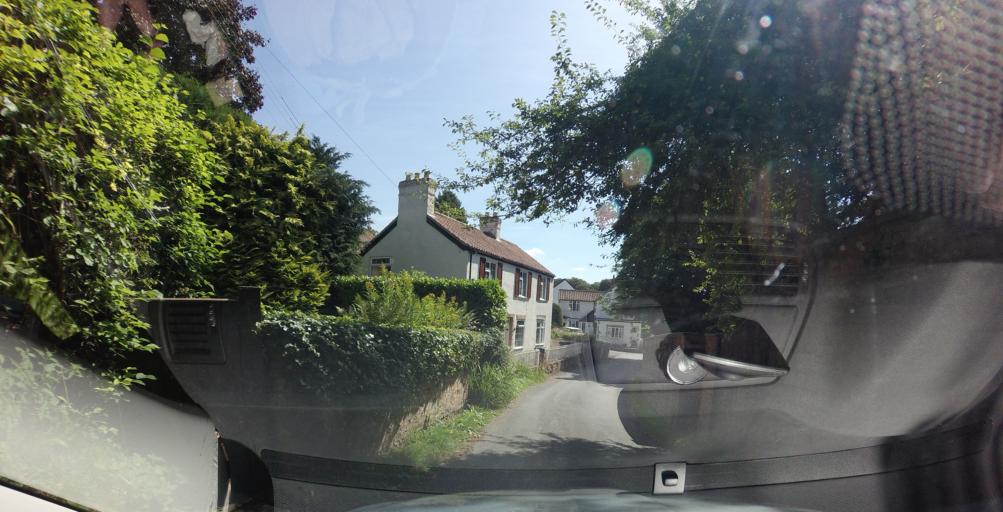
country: GB
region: England
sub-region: North Yorkshire
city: Ripon
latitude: 54.1417
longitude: -1.5025
